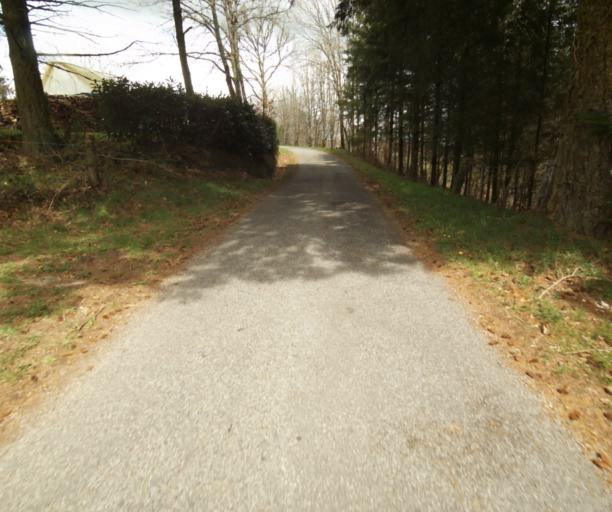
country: FR
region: Limousin
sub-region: Departement de la Correze
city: Correze
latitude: 45.3478
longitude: 1.9372
